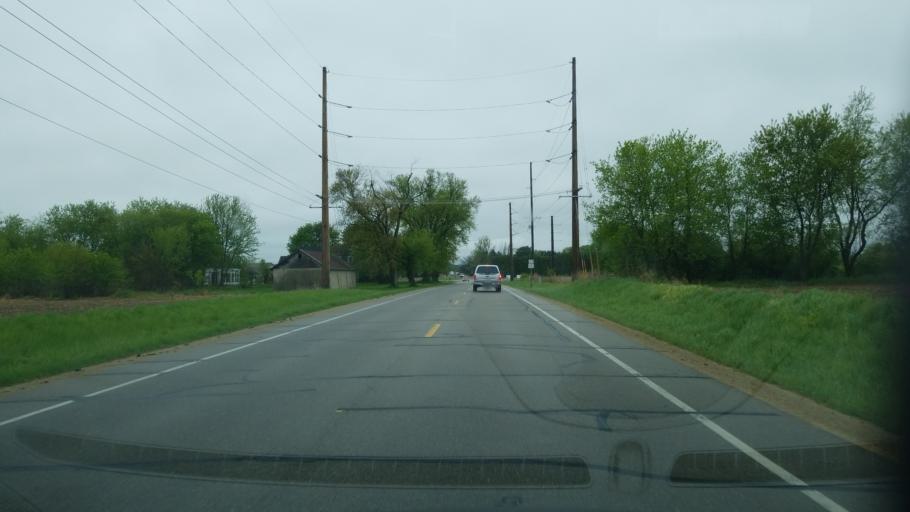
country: US
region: Wisconsin
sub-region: Dane County
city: Fitchburg
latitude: 42.9314
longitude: -89.4380
